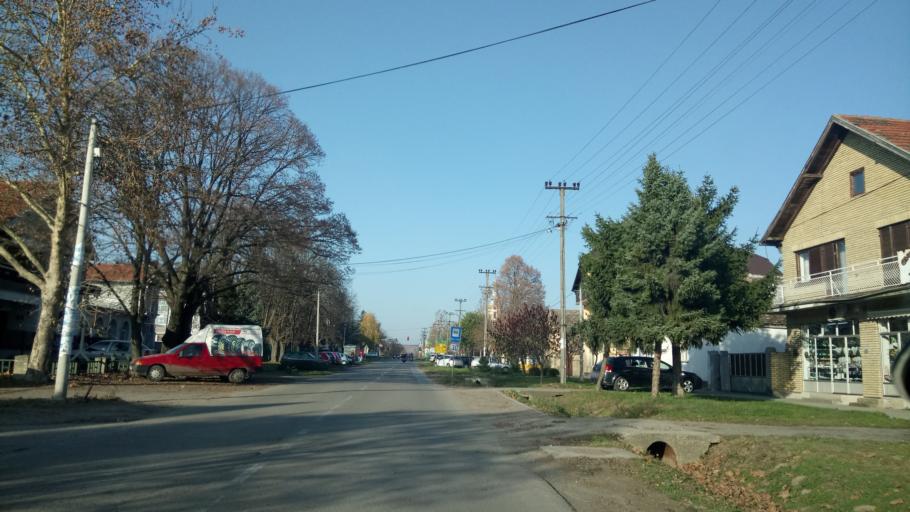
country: RS
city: Beska
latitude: 45.1280
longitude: 20.0674
